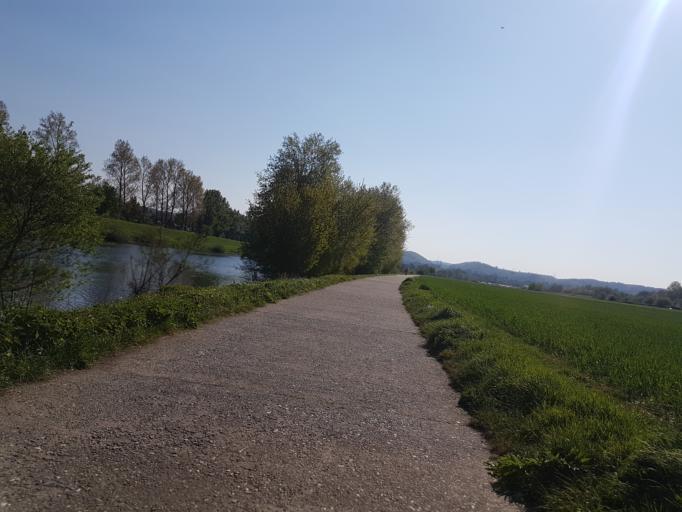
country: DE
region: North Rhine-Westphalia
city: Hattingen
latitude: 51.4115
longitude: 7.1818
